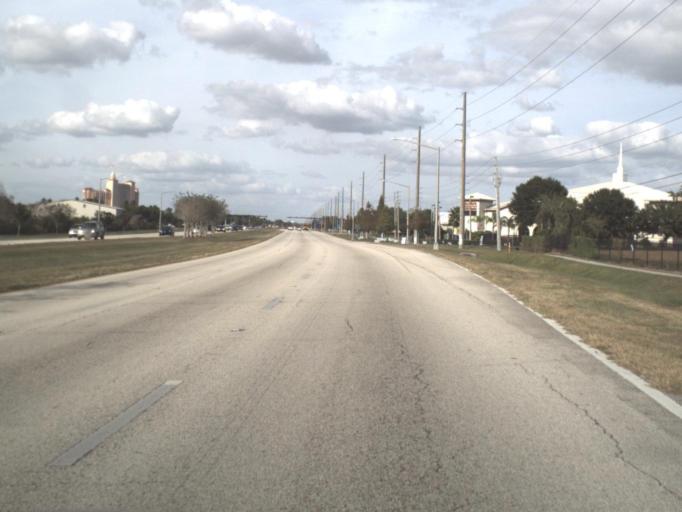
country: US
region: Florida
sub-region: Orange County
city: Hunters Creek
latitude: 28.3838
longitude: -81.4249
